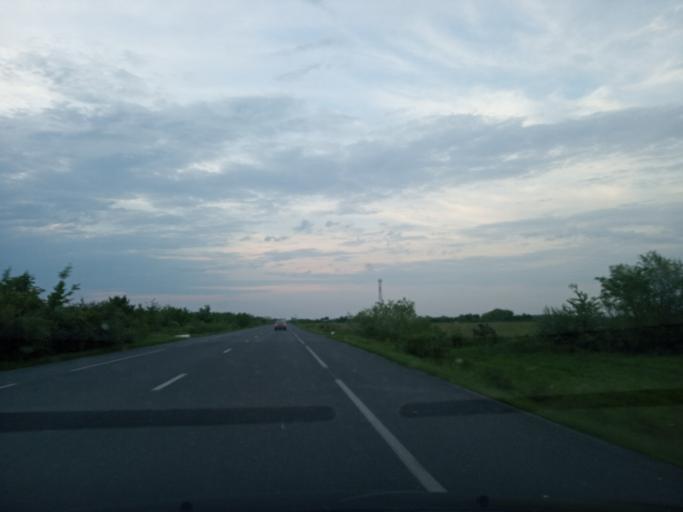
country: RO
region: Timis
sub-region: Oras Deta
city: Deta
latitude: 45.3799
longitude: 21.2328
